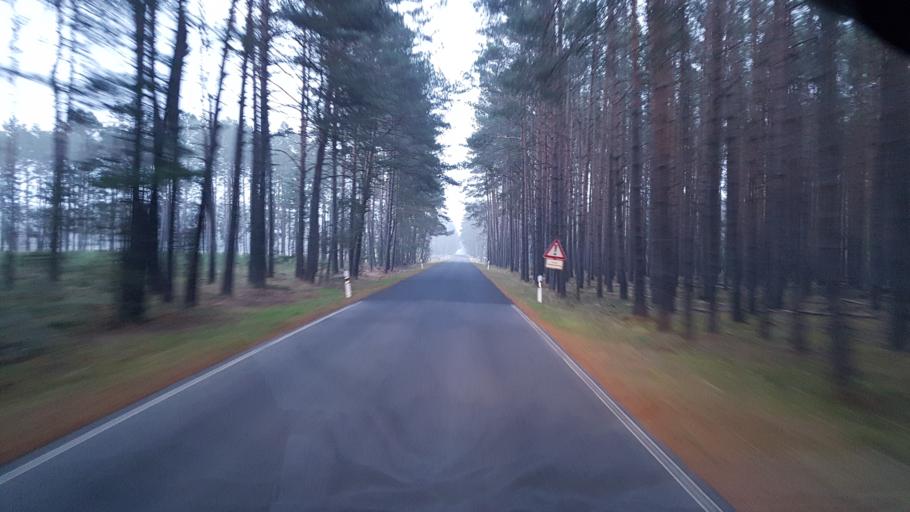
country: DE
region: Brandenburg
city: Bronkow
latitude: 51.6892
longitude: 13.9260
